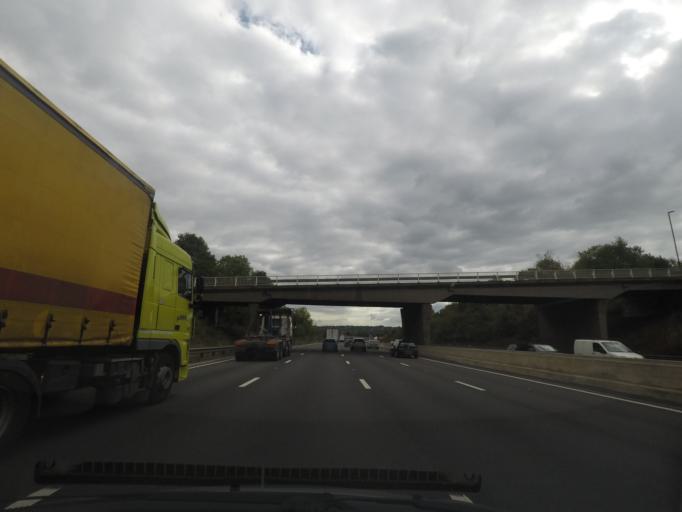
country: GB
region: England
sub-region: Sheffield
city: Chapletown
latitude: 53.4557
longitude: -1.4451
